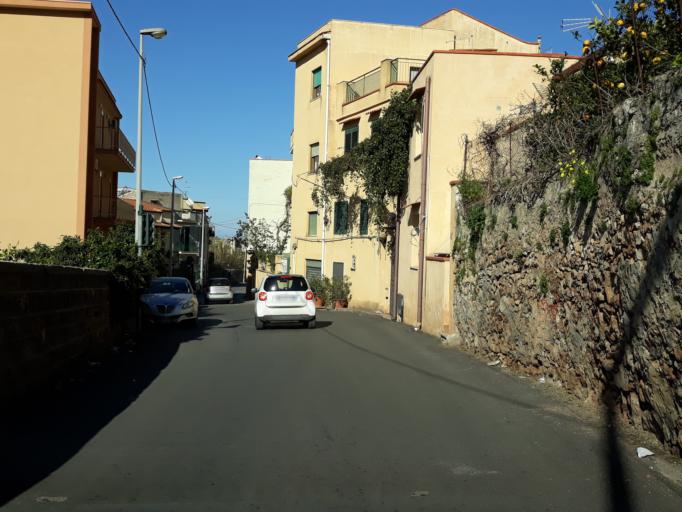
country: IT
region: Sicily
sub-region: Palermo
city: Ciaculli
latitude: 38.0834
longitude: 13.3767
